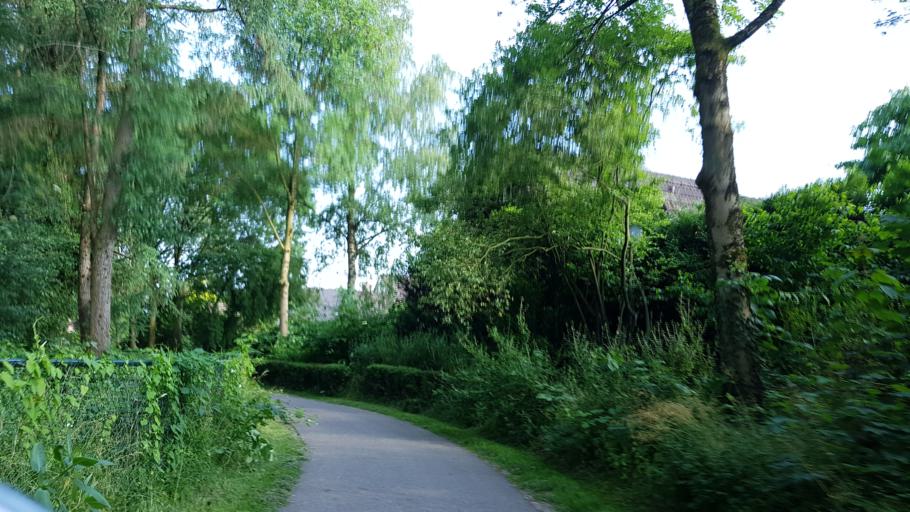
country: NL
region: Gelderland
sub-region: Gemeente Apeldoorn
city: Apeldoorn
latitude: 52.1958
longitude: 5.9959
